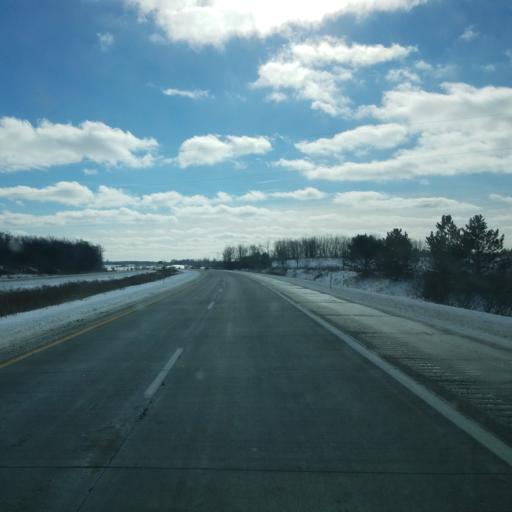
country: US
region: Michigan
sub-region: Clinton County
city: DeWitt
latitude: 42.8274
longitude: -84.5187
